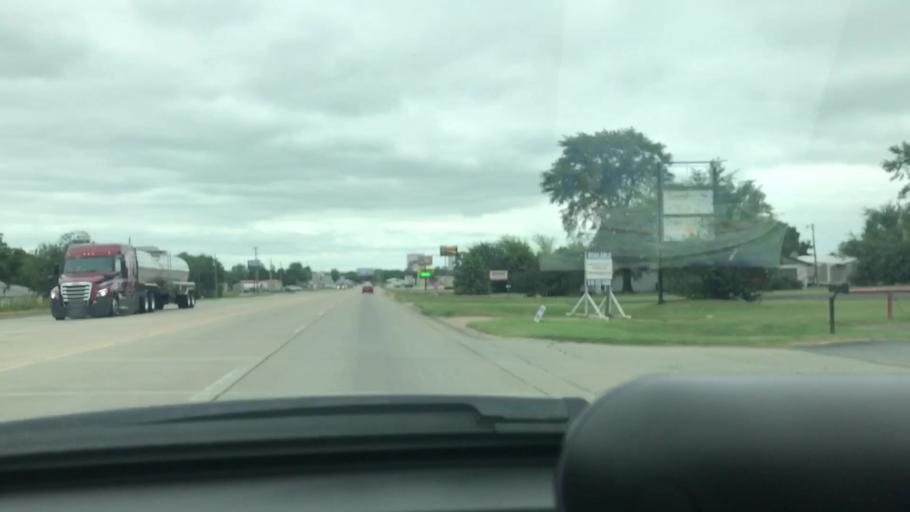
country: US
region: Oklahoma
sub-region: Mayes County
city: Chouteau
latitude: 36.1701
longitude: -95.3418
